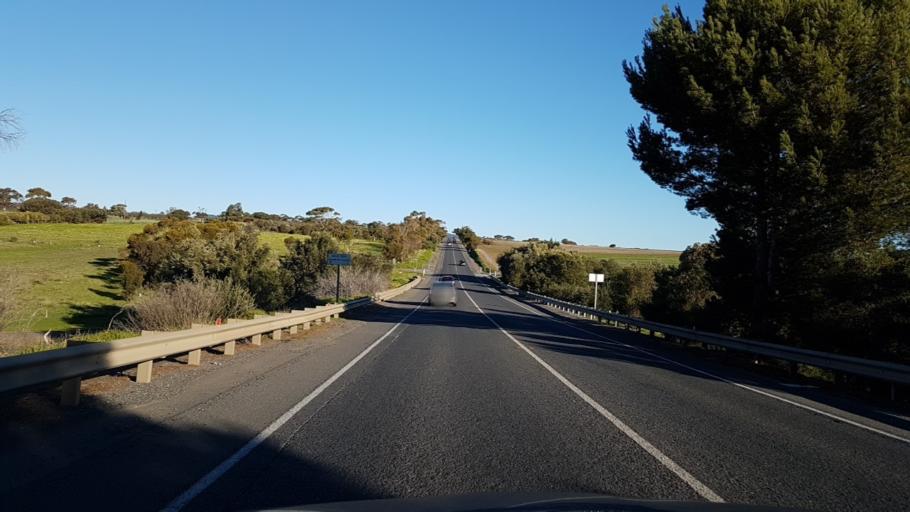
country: AU
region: South Australia
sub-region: Onkaparinga
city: Aldinga
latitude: -35.2427
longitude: 138.4940
